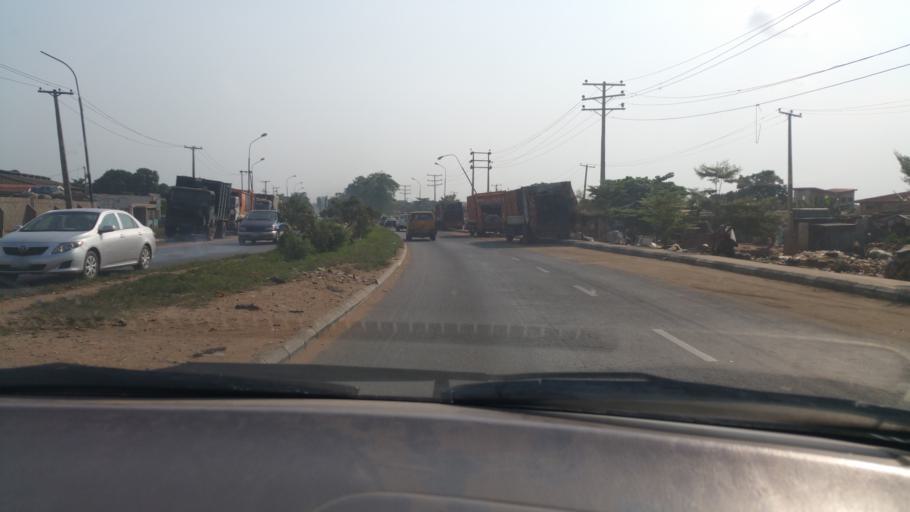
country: NG
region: Lagos
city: Ikotun
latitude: 6.5710
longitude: 3.2526
